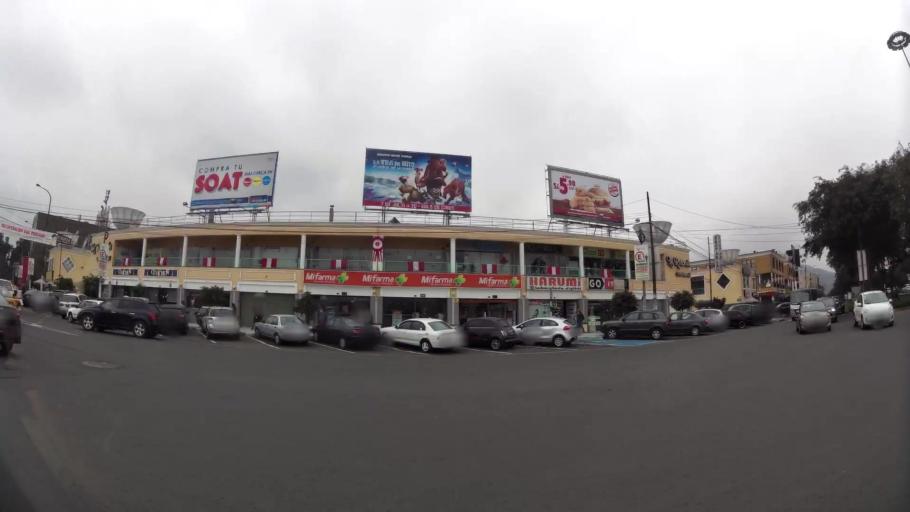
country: PE
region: Lima
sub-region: Lima
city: La Molina
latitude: -12.0735
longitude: -76.9556
